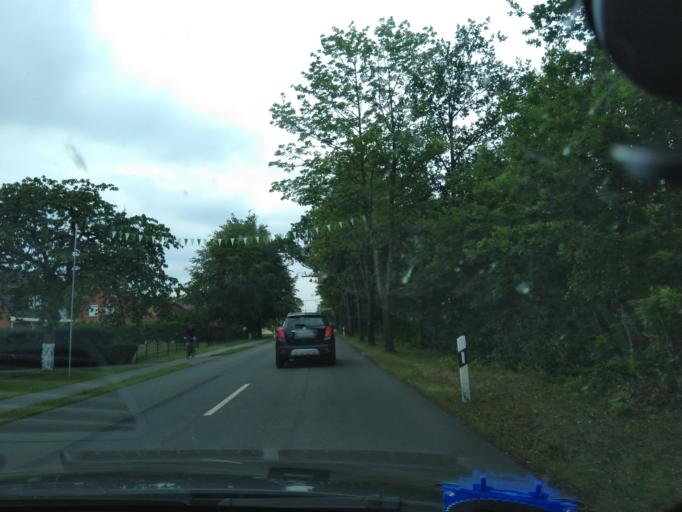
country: DE
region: Lower Saxony
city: Twist
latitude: 52.6418
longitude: 7.0984
